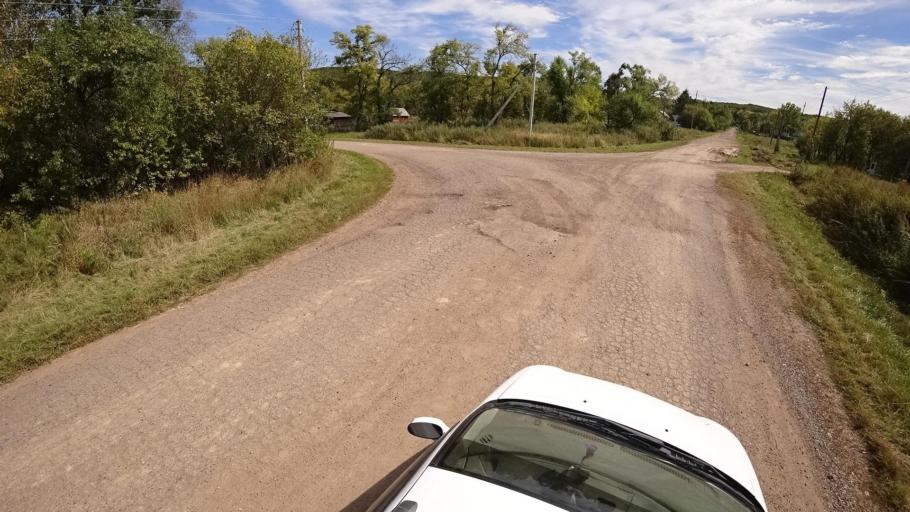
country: RU
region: Primorskiy
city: Yakovlevka
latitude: 44.6555
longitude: 133.7437
